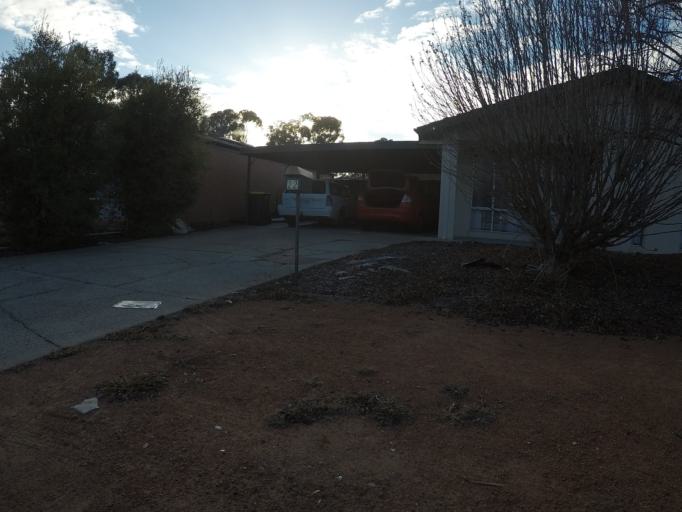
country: AU
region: Australian Capital Territory
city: Macarthur
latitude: -35.4245
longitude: 149.0977
